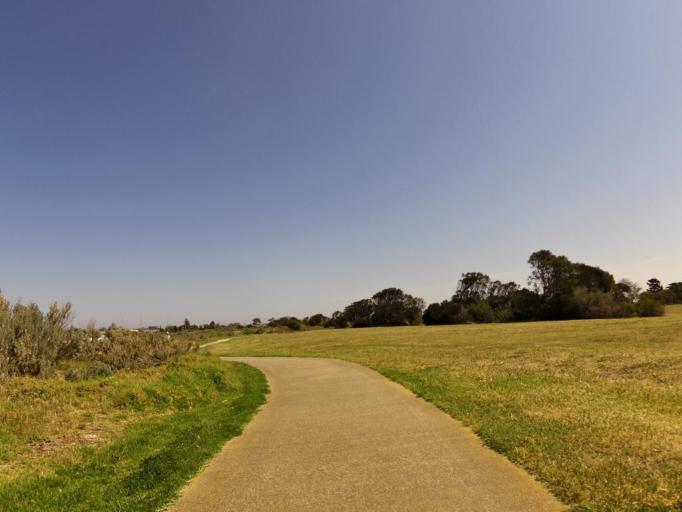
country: AU
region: Victoria
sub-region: Hobsons Bay
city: Seaholme
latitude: -37.8630
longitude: 144.8537
